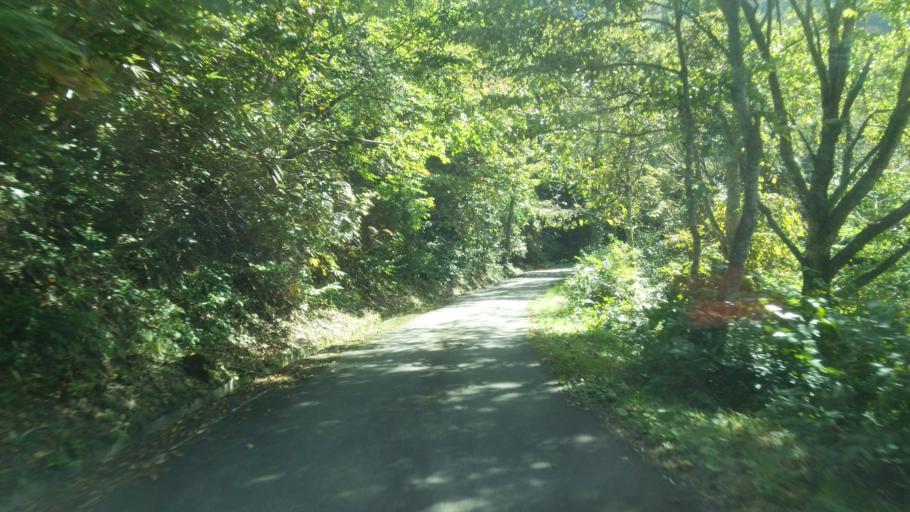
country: JP
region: Fukushima
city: Kitakata
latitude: 37.6107
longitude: 139.9888
